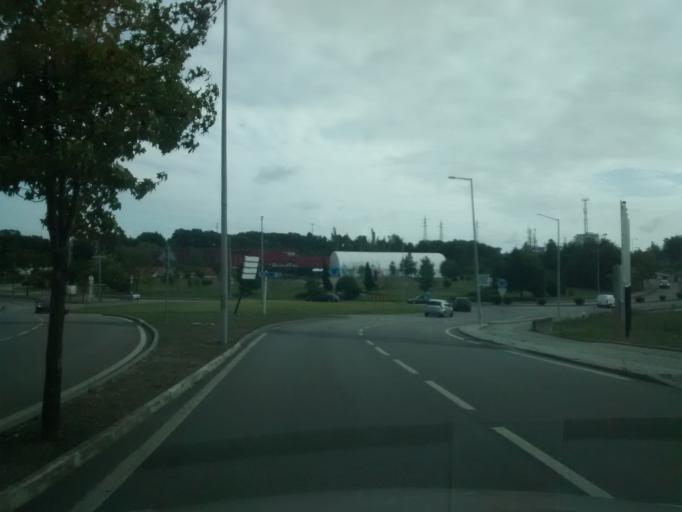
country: PT
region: Aveiro
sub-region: Aveiro
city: Aveiro
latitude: 40.6393
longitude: -8.6409
